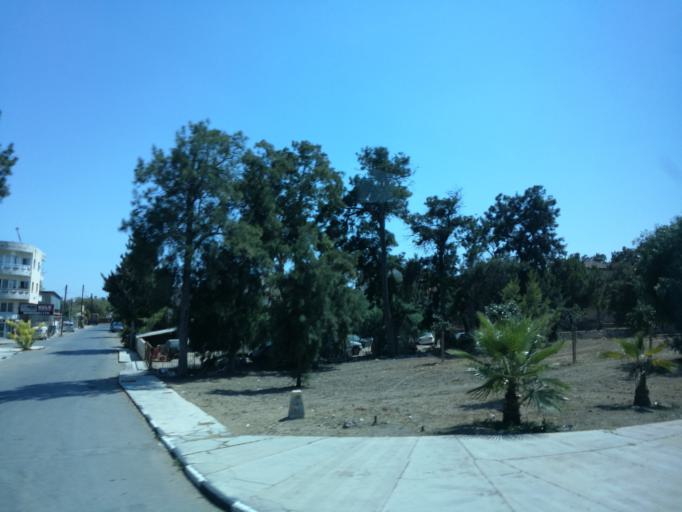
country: CY
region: Ammochostos
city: Famagusta
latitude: 35.1209
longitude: 33.9456
